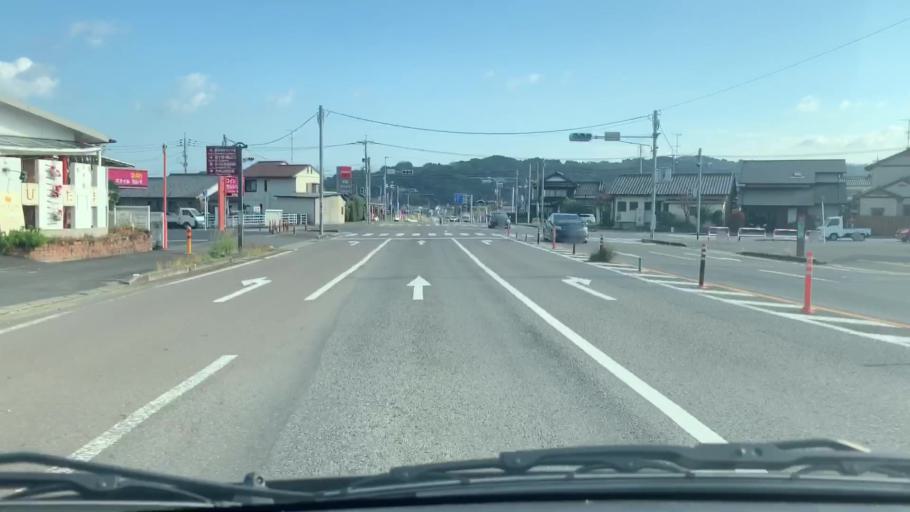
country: JP
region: Saga Prefecture
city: Kashima
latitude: 33.0953
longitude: 130.0929
